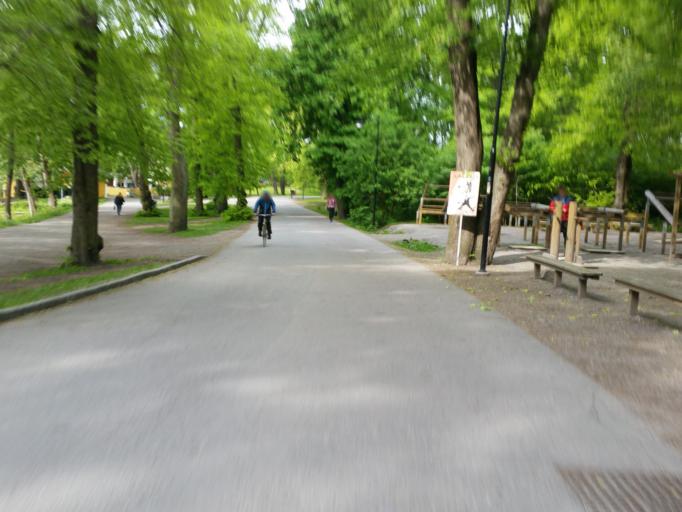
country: SE
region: Stockholm
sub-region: Stockholms Kommun
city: Arsta
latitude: 59.3046
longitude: 18.0740
